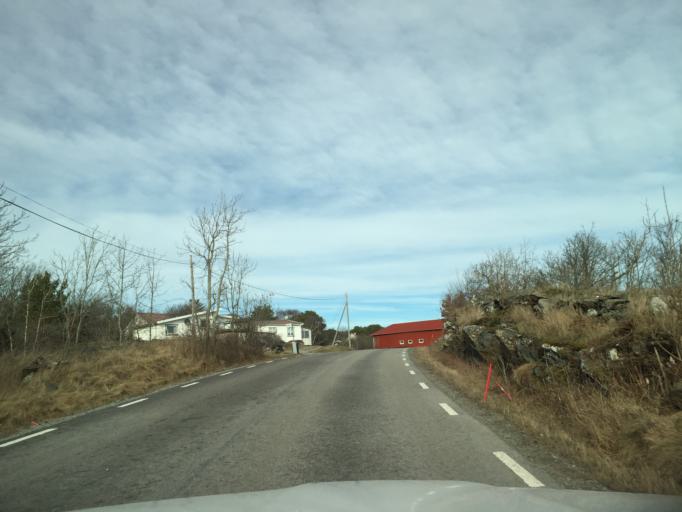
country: SE
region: Vaestra Goetaland
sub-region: Tjorns Kommun
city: Skaerhamn
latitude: 58.0206
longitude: 11.5338
